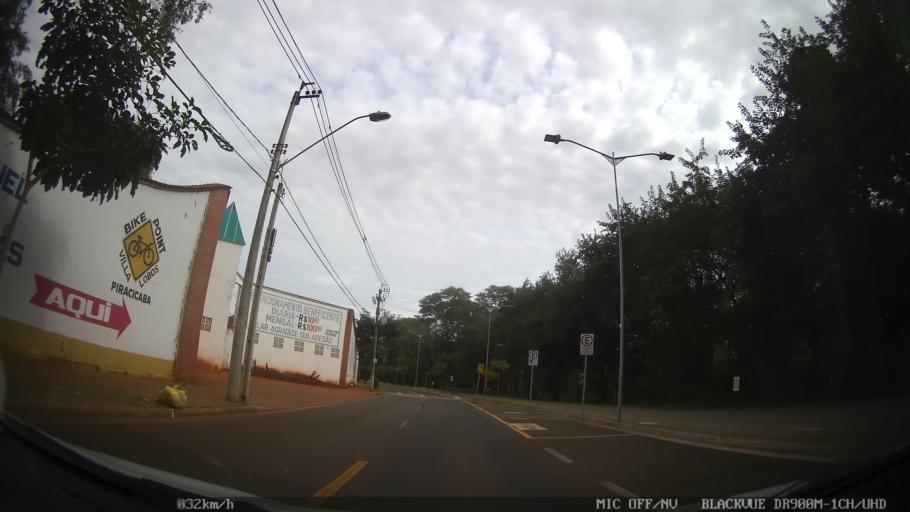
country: BR
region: Sao Paulo
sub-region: Piracicaba
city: Piracicaba
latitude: -22.7072
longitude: -47.6498
